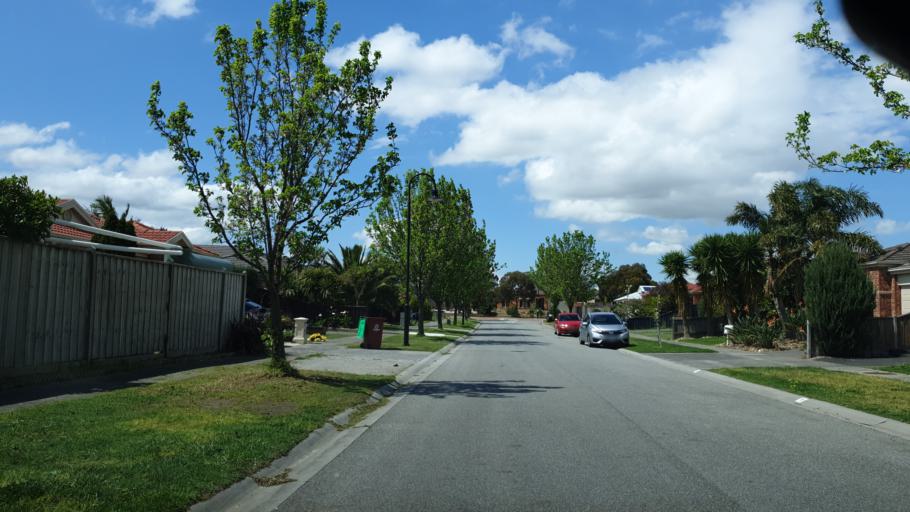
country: AU
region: Victoria
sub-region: Casey
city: Cranbourne North
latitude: -38.0737
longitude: 145.2935
